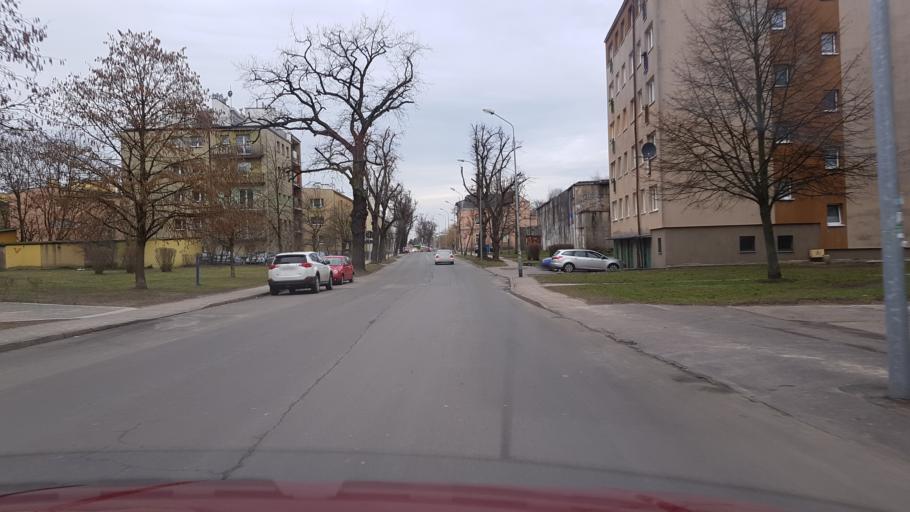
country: PL
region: West Pomeranian Voivodeship
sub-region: Powiat policki
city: Police
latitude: 53.5481
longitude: 14.5728
